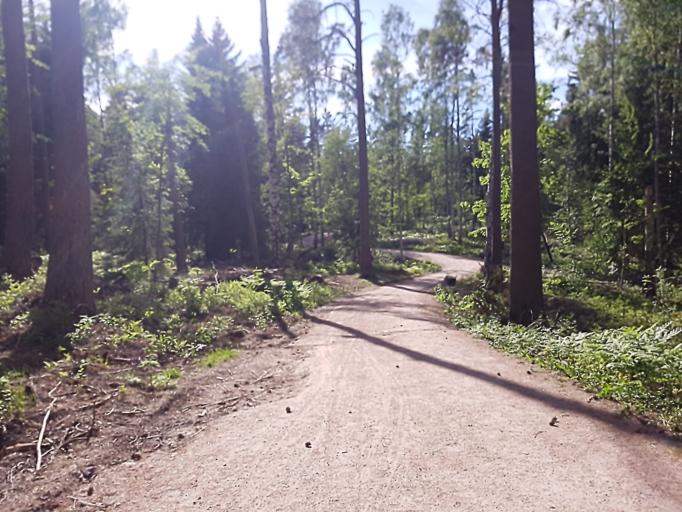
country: FI
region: Uusimaa
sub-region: Helsinki
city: Helsinki
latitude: 60.2385
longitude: 24.9590
